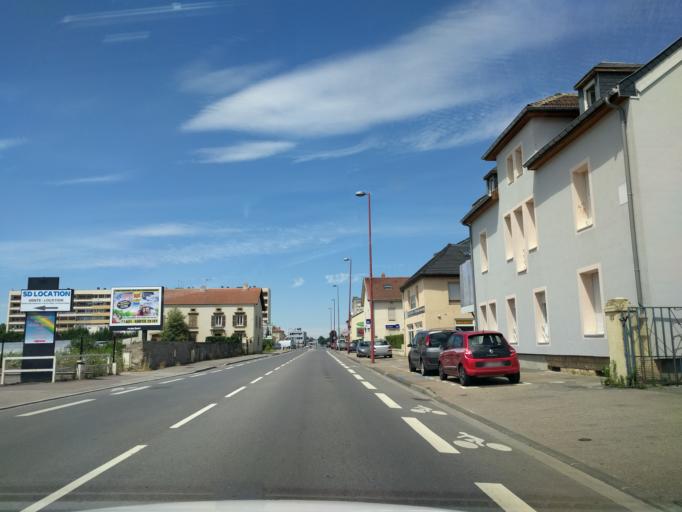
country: FR
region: Lorraine
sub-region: Departement de la Moselle
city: Metz
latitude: 49.1387
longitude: 6.1672
